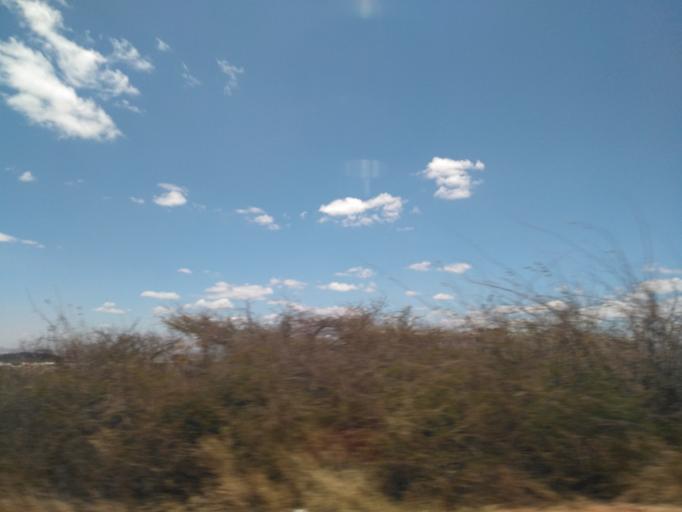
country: TZ
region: Dodoma
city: Kisasa
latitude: -6.2220
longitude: 35.7824
